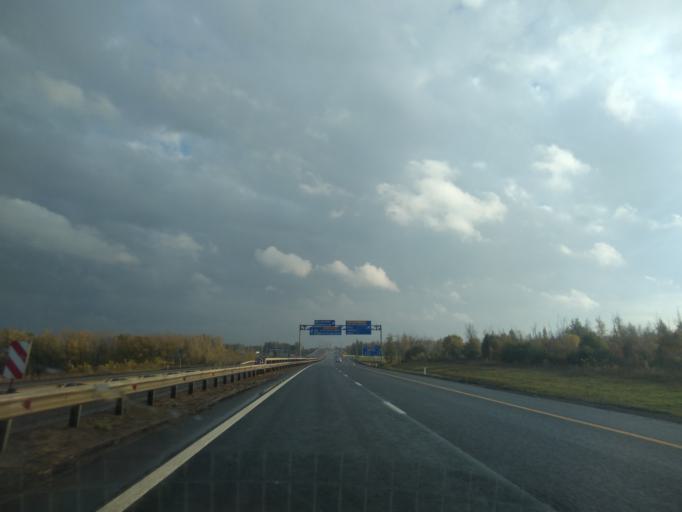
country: RU
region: Lipetsk
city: Yelets
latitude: 52.5546
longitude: 38.7158
